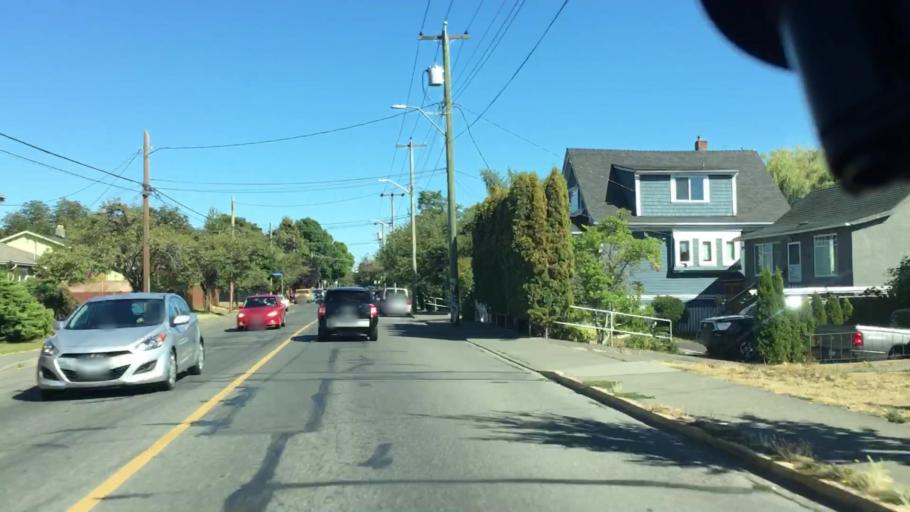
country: CA
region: British Columbia
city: Victoria
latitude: 48.4343
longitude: -123.3422
